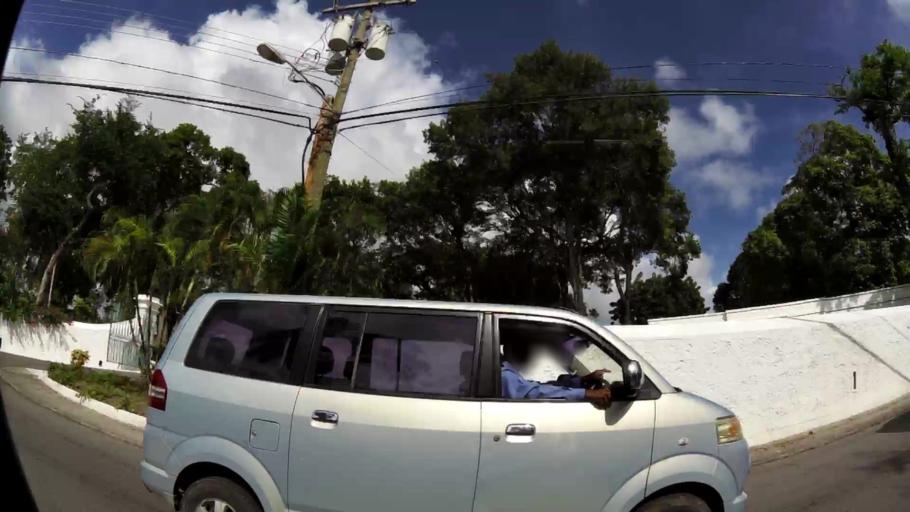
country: BB
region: Saint Michael
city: Bridgetown
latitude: 13.1004
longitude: -59.6001
